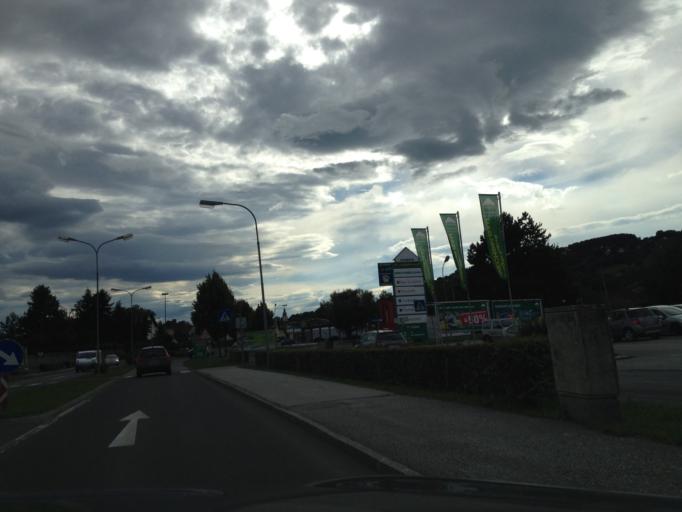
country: AT
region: Styria
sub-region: Politischer Bezirk Hartberg-Fuerstenfeld
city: Hartberg
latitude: 47.2834
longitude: 15.9871
